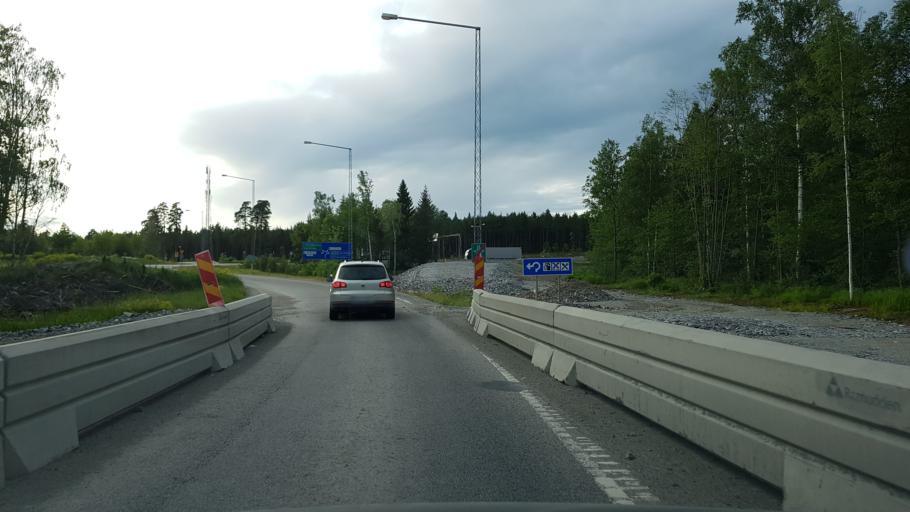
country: SE
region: Stockholm
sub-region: Jarfalla Kommun
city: Jakobsberg
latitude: 59.4722
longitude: 17.8143
